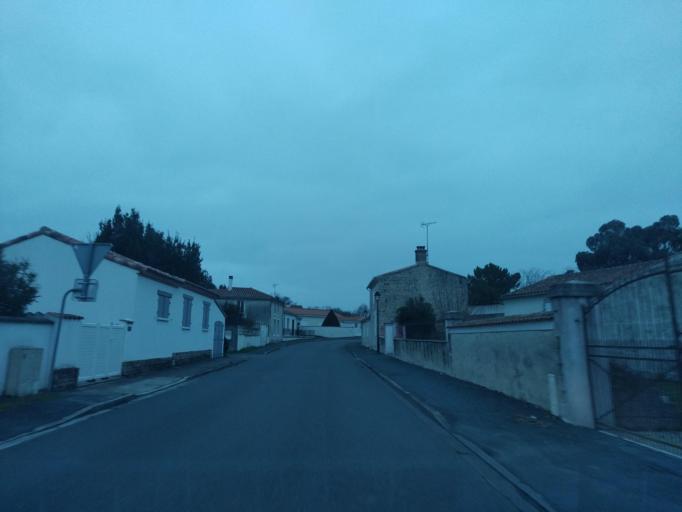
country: FR
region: Pays de la Loire
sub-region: Departement de la Vendee
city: Triaize
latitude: 46.3577
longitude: -1.2494
